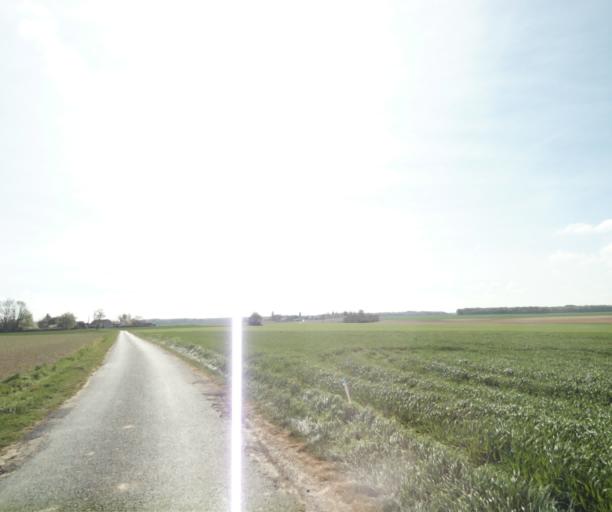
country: FR
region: Ile-de-France
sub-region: Departement de Seine-et-Marne
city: Nangis
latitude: 48.5356
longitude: 3.0396
